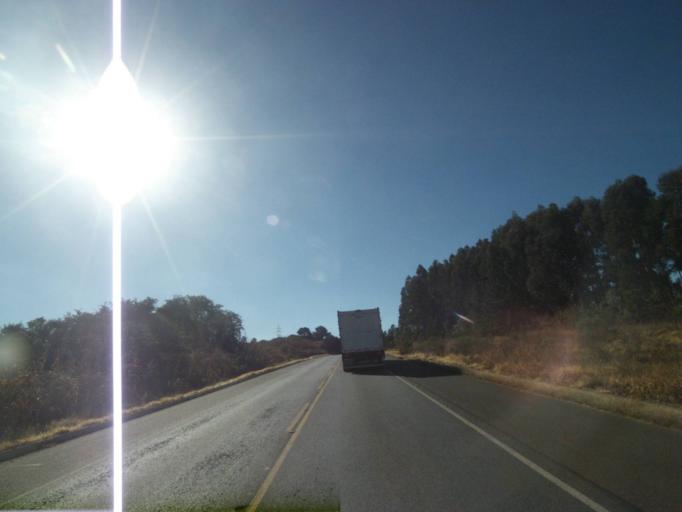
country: BR
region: Parana
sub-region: Tibagi
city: Tibagi
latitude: -24.5314
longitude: -50.4477
